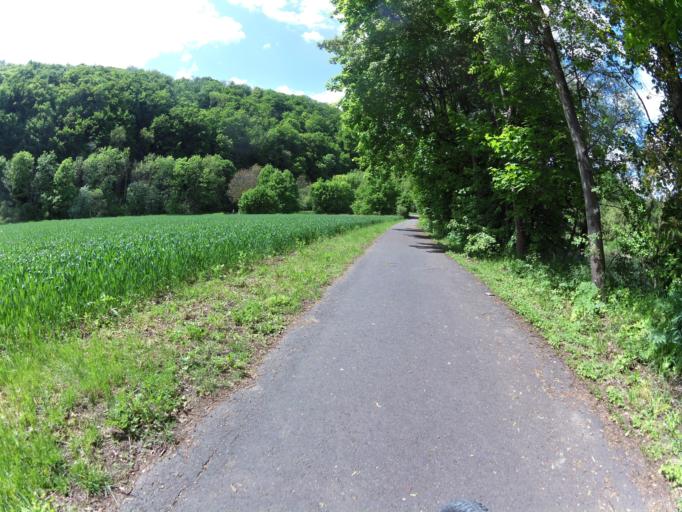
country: DE
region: Thuringia
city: Ebenshausen
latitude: 51.0852
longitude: 10.3083
